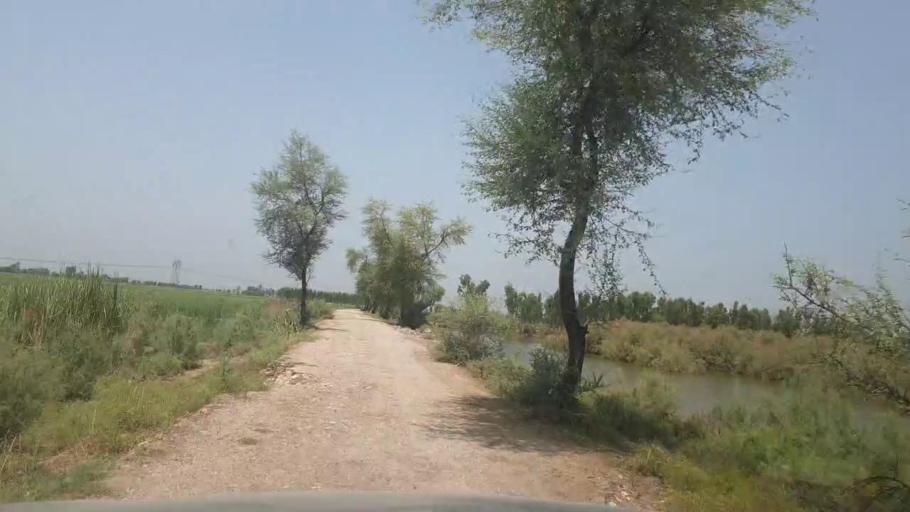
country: PK
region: Sindh
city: Lakhi
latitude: 27.8574
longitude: 68.6245
